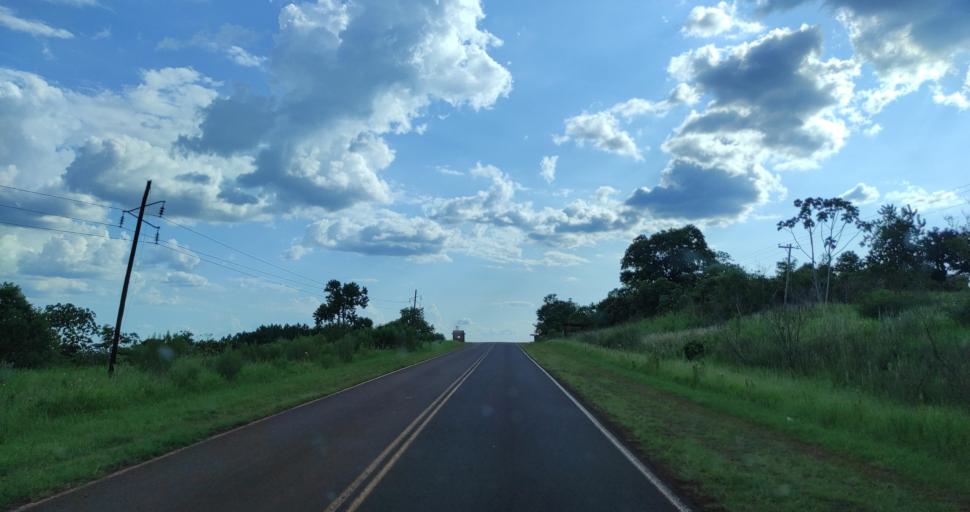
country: AR
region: Misiones
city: San Vicente
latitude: -26.3381
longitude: -54.1768
